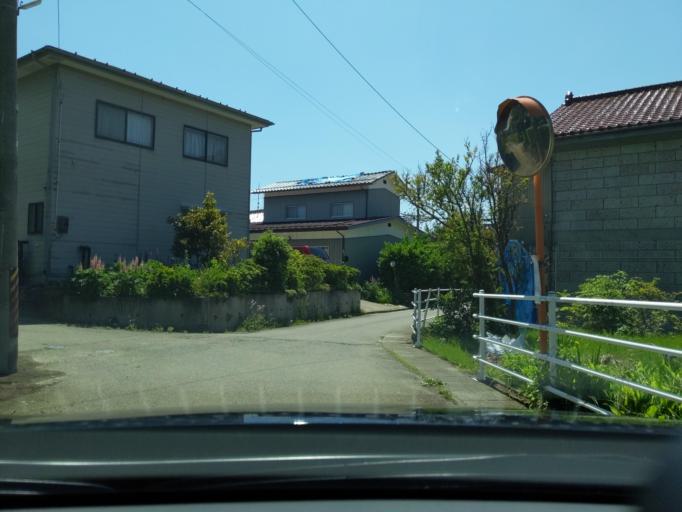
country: JP
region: Fukushima
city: Koriyama
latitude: 37.3977
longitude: 140.2720
